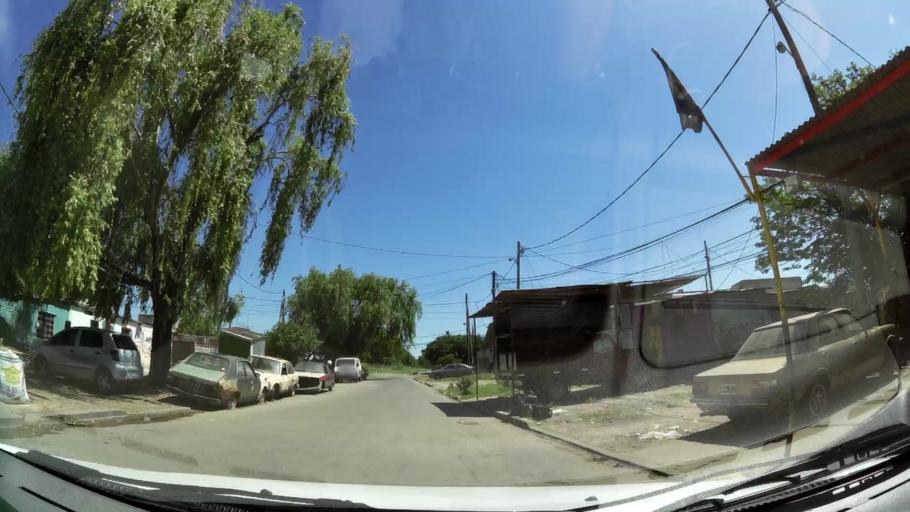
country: AR
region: Buenos Aires
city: Caseros
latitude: -34.5655
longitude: -58.5778
